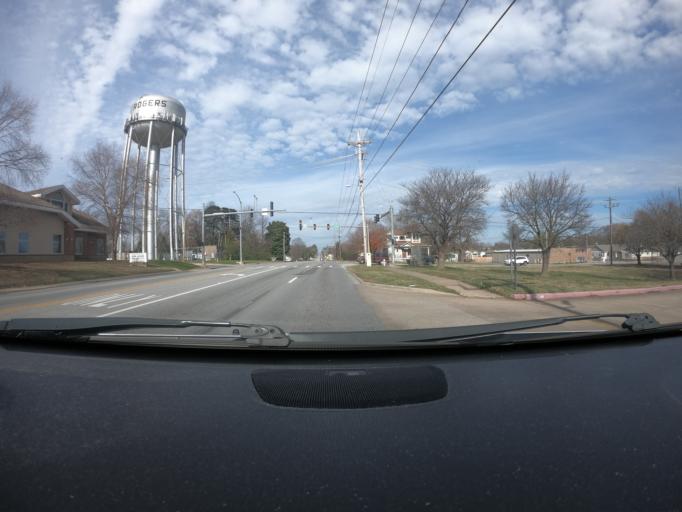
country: US
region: Arkansas
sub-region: Benton County
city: Rogers
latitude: 36.3366
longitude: -94.1257
